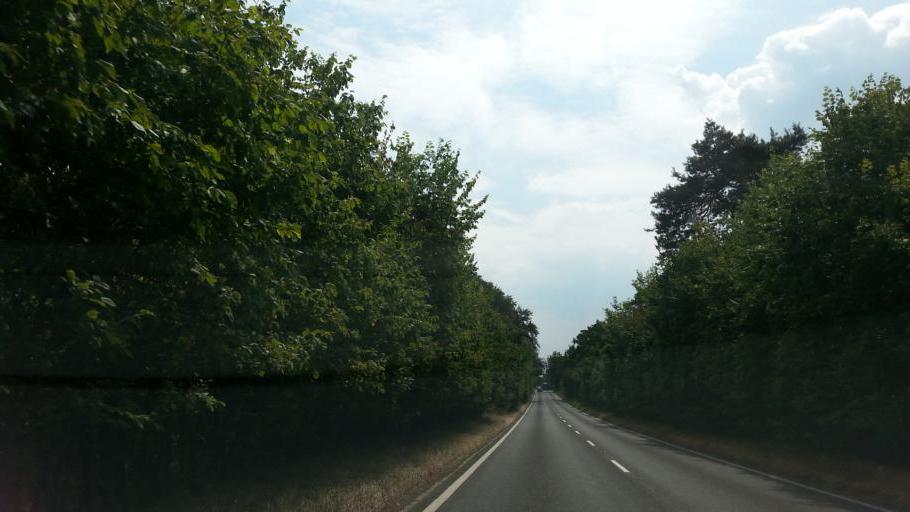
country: GB
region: England
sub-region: Suffolk
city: Lakenheath
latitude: 52.3648
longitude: 0.5398
